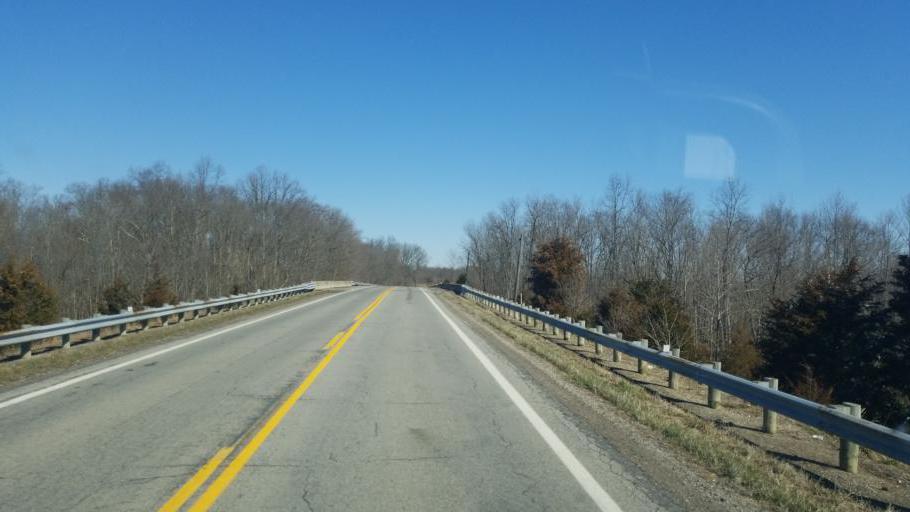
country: US
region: Ohio
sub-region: Highland County
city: Greenfield
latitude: 39.3466
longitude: -83.3669
